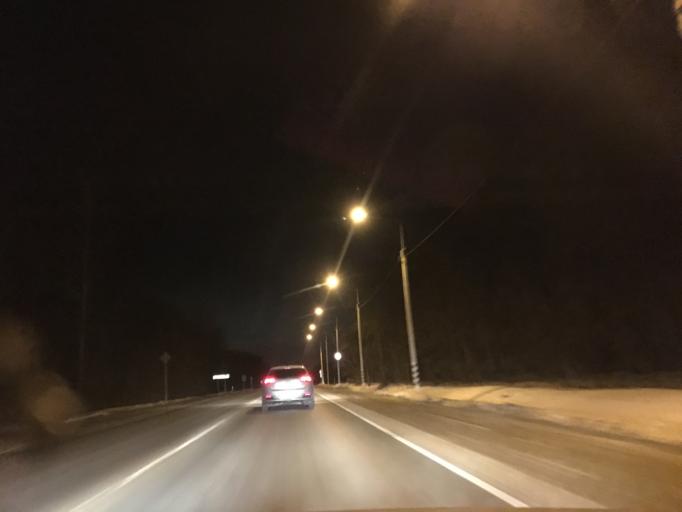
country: RU
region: Tula
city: Kosaya Gora
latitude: 54.0847
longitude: 37.5450
